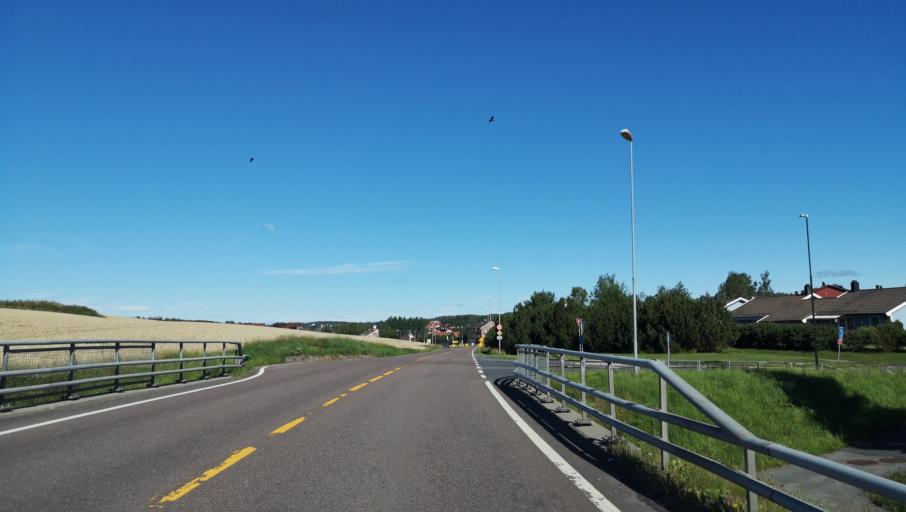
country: NO
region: Ostfold
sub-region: Spydeberg
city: Spydeberg
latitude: 59.6124
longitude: 11.0858
